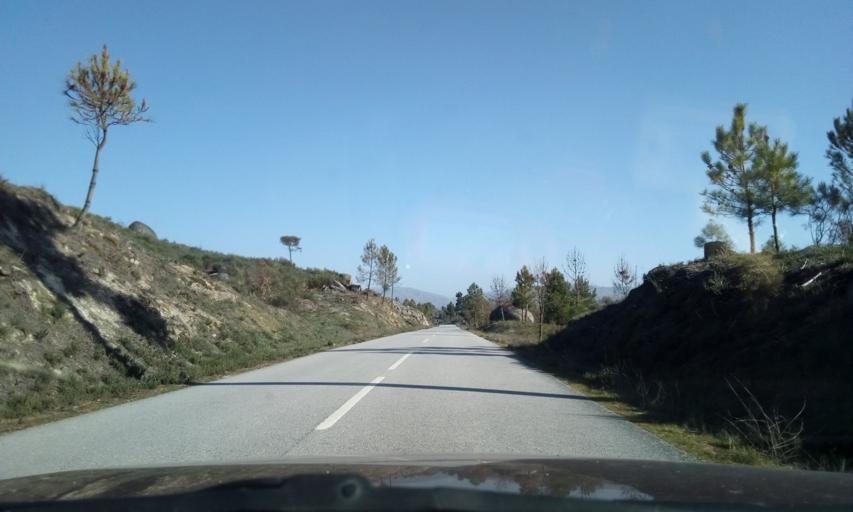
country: PT
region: Guarda
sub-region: Fornos de Algodres
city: Fornos de Algodres
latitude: 40.6423
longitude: -7.4738
